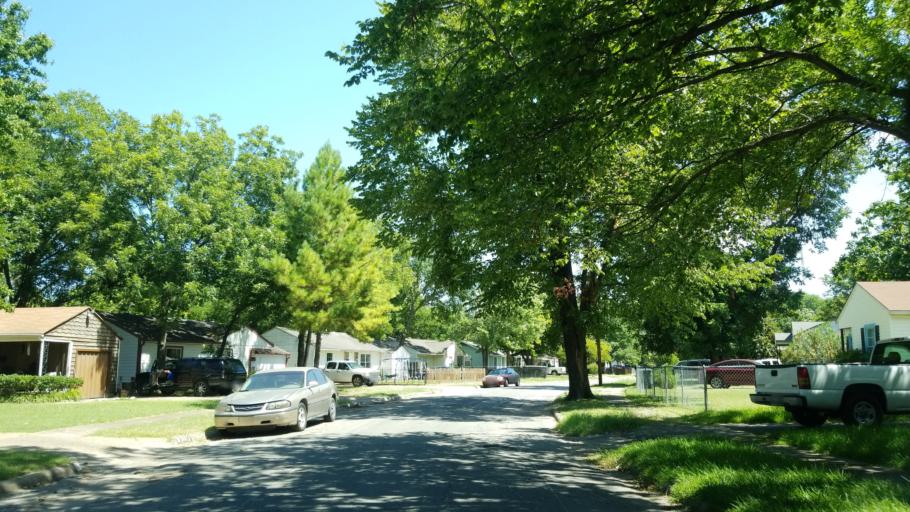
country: US
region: Texas
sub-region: Dallas County
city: Balch Springs
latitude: 32.7350
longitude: -96.6942
